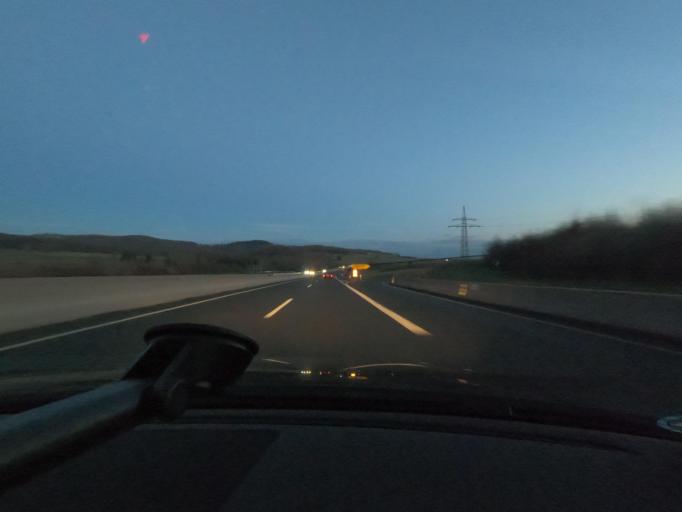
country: DE
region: Lower Saxony
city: Bad Lauterberg im Harz
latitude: 51.6103
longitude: 10.4646
